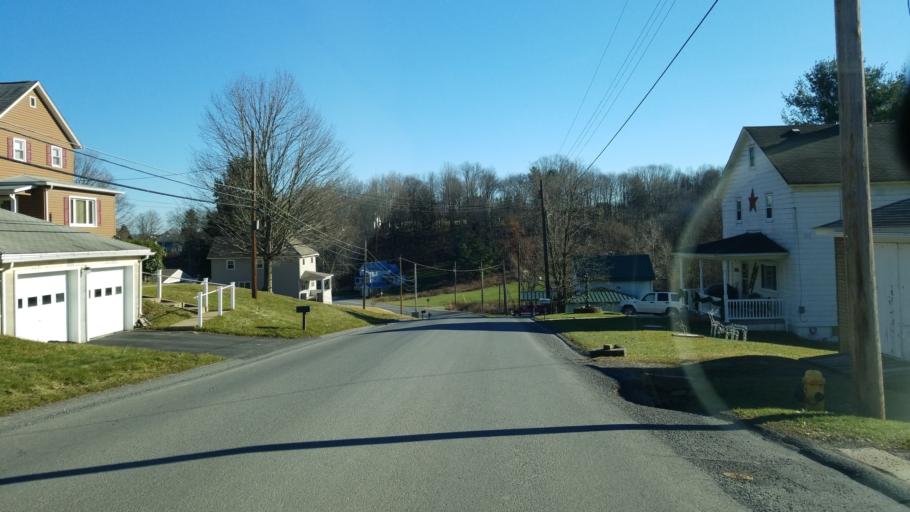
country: US
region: Pennsylvania
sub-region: Clearfield County
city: Sandy
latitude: 41.1250
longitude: -78.7820
